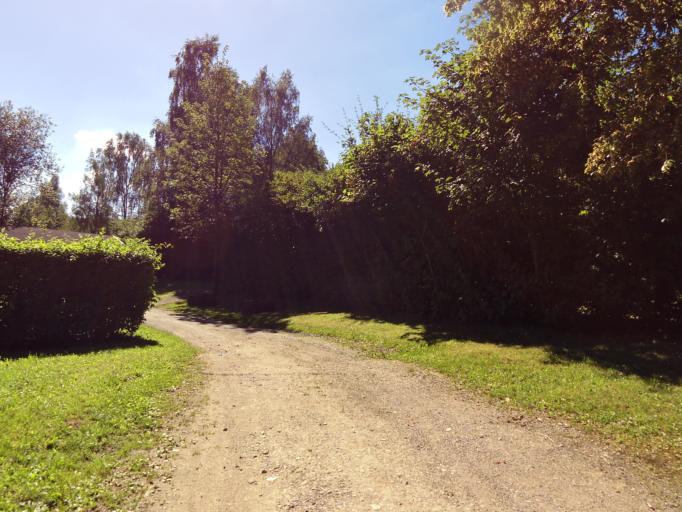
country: DE
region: Hesse
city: Reichelsheim
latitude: 49.6412
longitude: 8.8946
